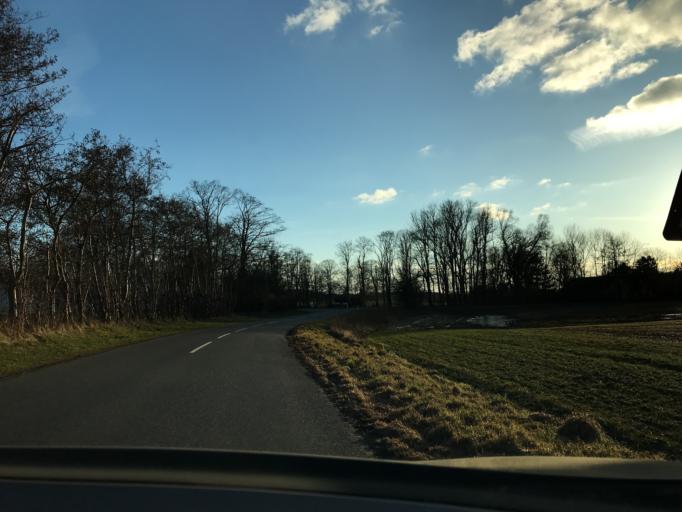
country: DK
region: South Denmark
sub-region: Middelfart Kommune
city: Brenderup
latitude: 55.5110
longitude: 10.0251
